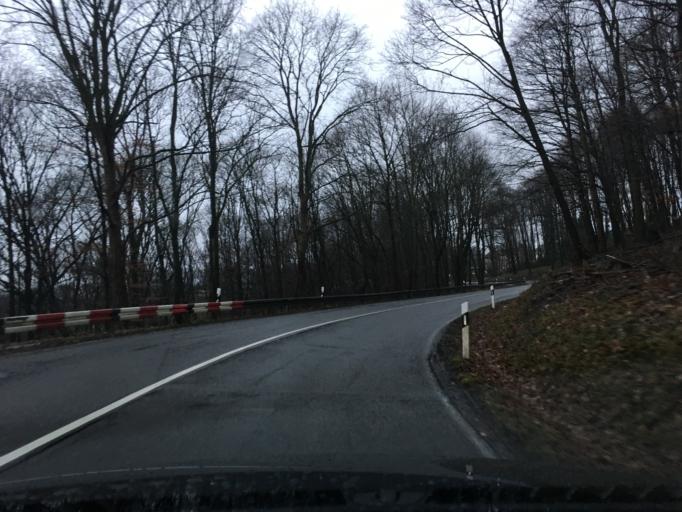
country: DE
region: North Rhine-Westphalia
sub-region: Regierungsbezirk Dusseldorf
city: Velbert
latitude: 51.3073
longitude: 7.0747
